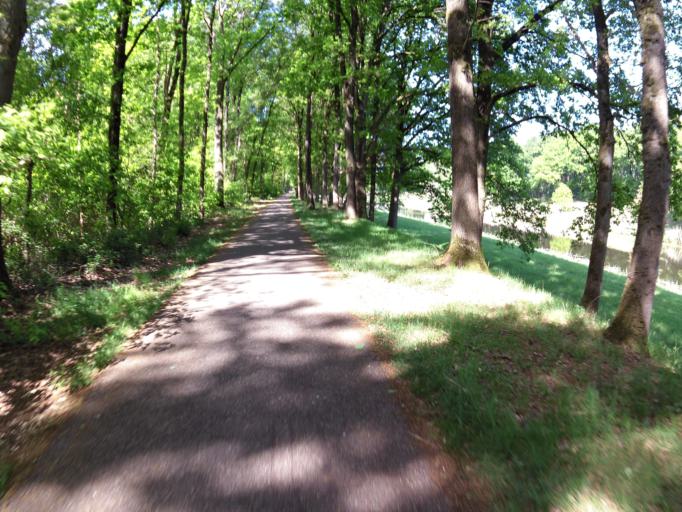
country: NL
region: North Brabant
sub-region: Gemeente Waalwijk
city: Waalwijk
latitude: 51.6687
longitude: 5.1341
